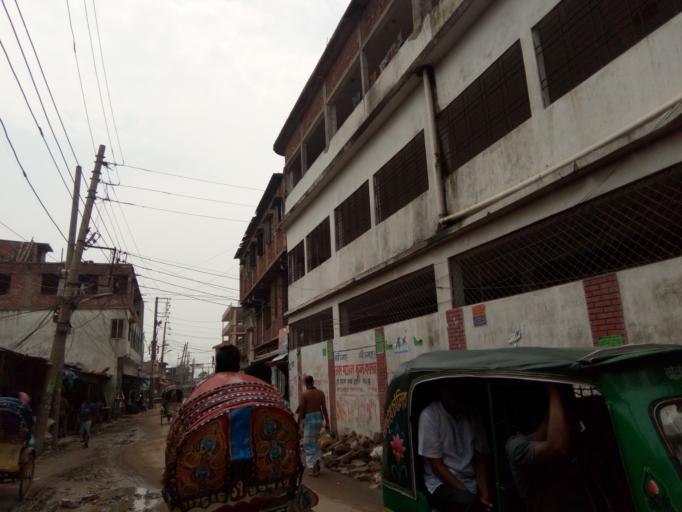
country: BD
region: Dhaka
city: Azimpur
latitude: 23.7111
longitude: 90.3638
